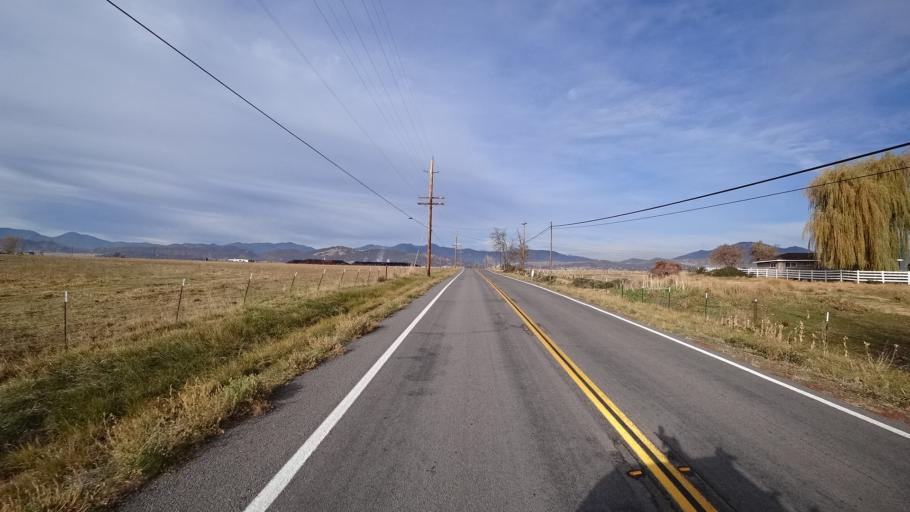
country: US
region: California
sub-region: Siskiyou County
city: Montague
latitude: 41.7313
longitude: -122.5809
